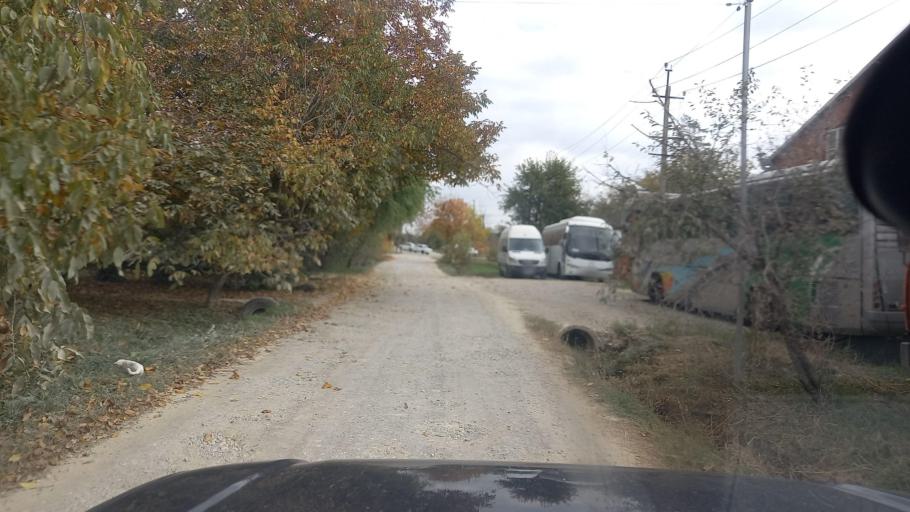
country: RU
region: Krasnodarskiy
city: Il'skiy
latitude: 44.8482
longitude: 38.5577
